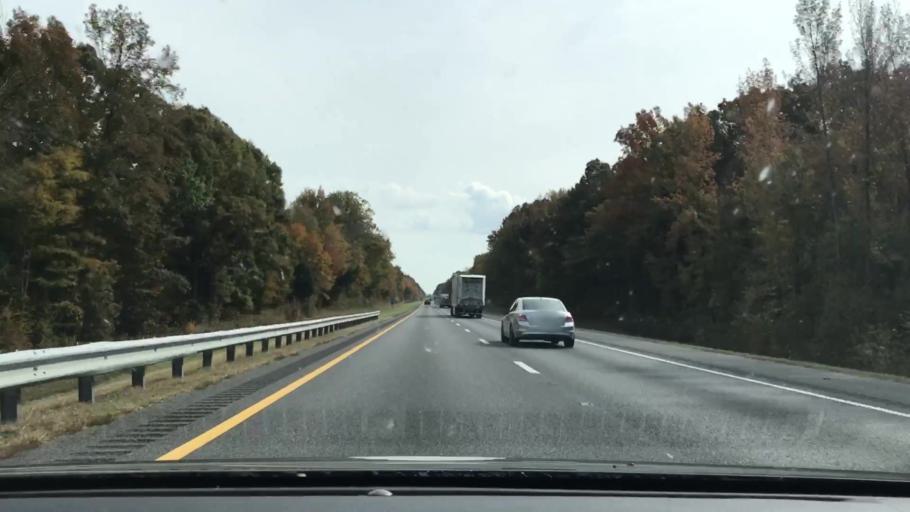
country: US
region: Kentucky
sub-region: Todd County
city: Guthrie
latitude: 36.5021
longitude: -87.1871
